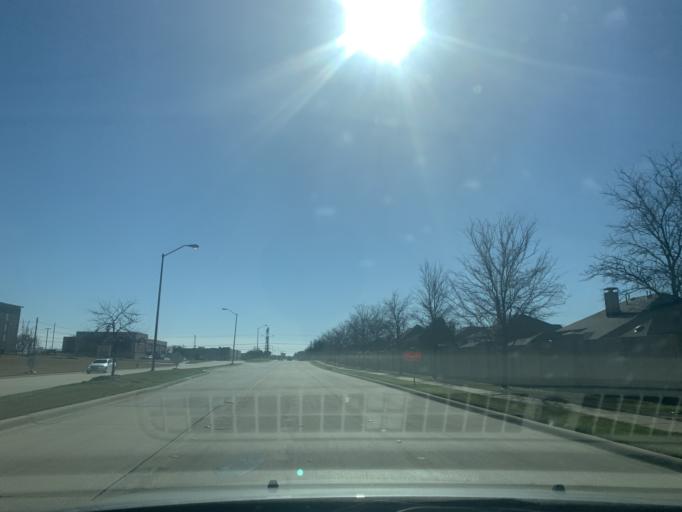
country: US
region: Texas
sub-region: Denton County
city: The Colony
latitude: 33.0645
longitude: -96.8329
